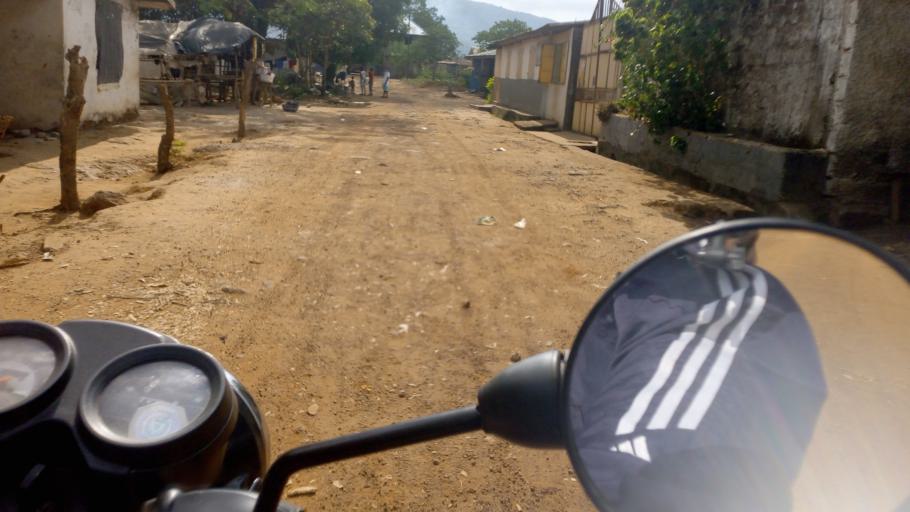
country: SL
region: Western Area
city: Waterloo
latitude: 8.3221
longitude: -13.0817
